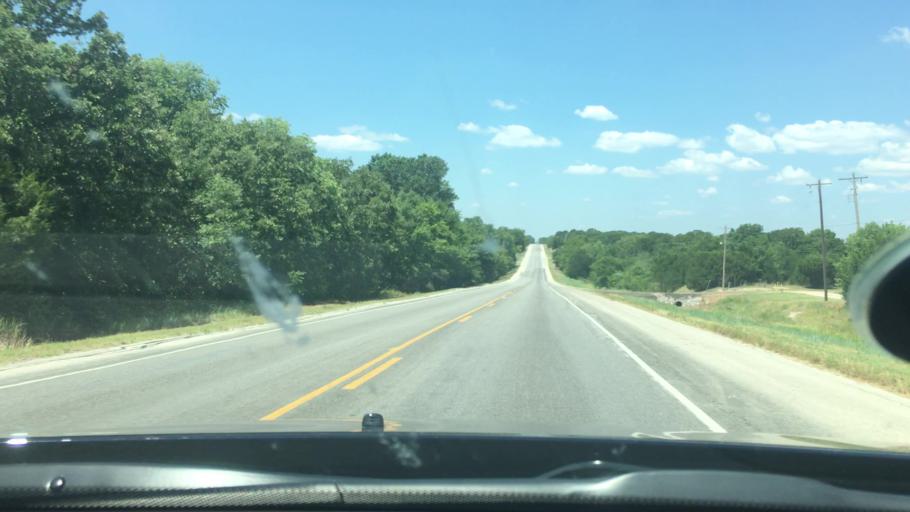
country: US
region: Oklahoma
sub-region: Carter County
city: Dickson
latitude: 34.1873
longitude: -96.9163
